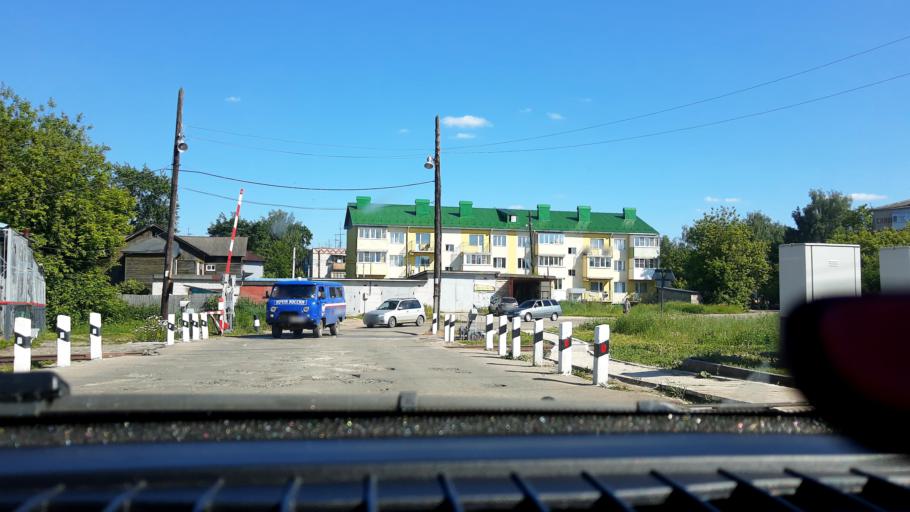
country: RU
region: Nizjnij Novgorod
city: Gidrotorf
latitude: 56.5234
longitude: 43.5449
